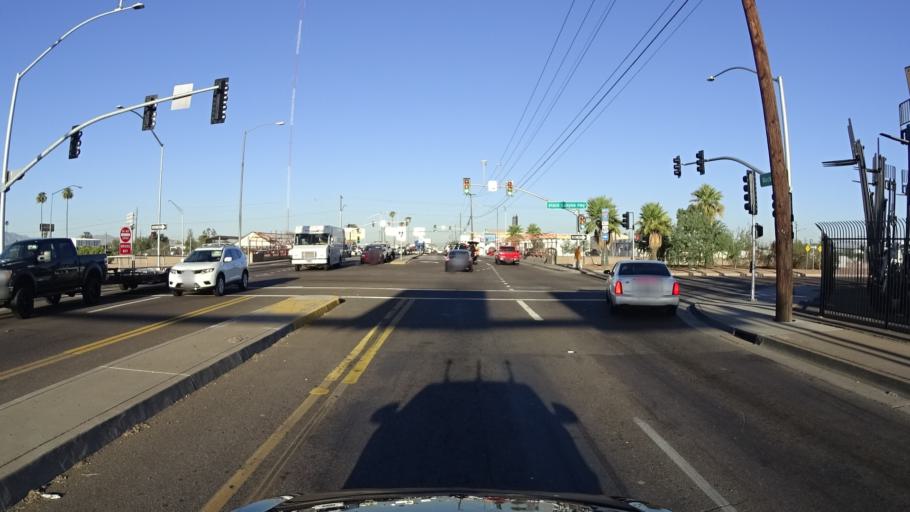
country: US
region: Arizona
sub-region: Maricopa County
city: Phoenix
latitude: 33.4368
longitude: -112.1073
